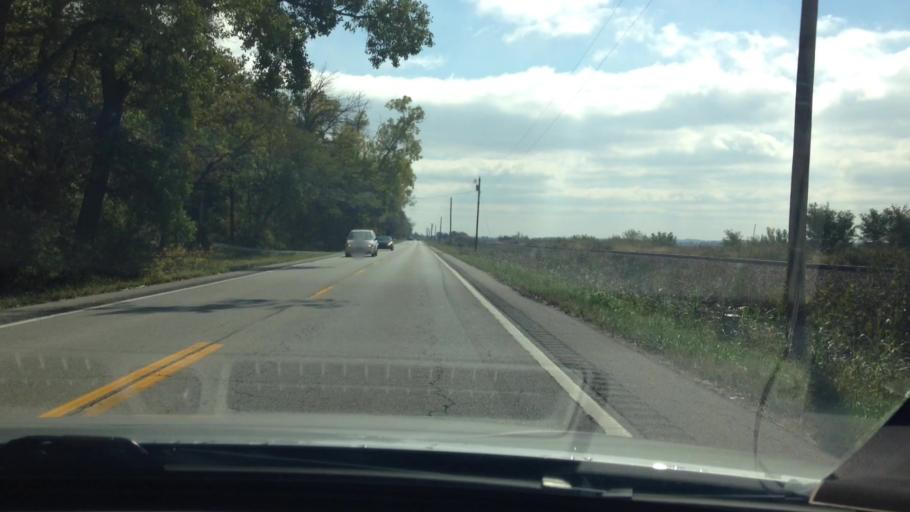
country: US
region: Kansas
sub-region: Leavenworth County
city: Lansing
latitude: 39.2974
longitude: -94.8445
